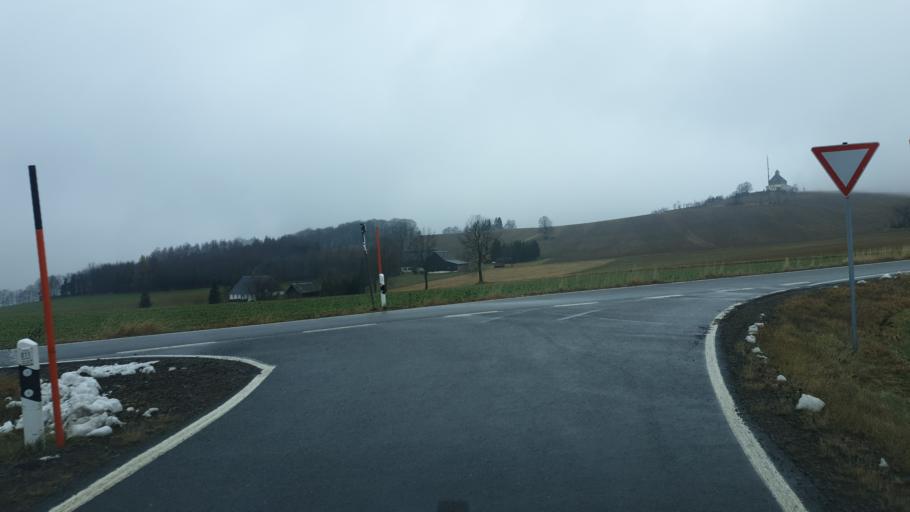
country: DE
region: Saxony
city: Neuhausen
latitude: 50.6565
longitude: 13.4750
